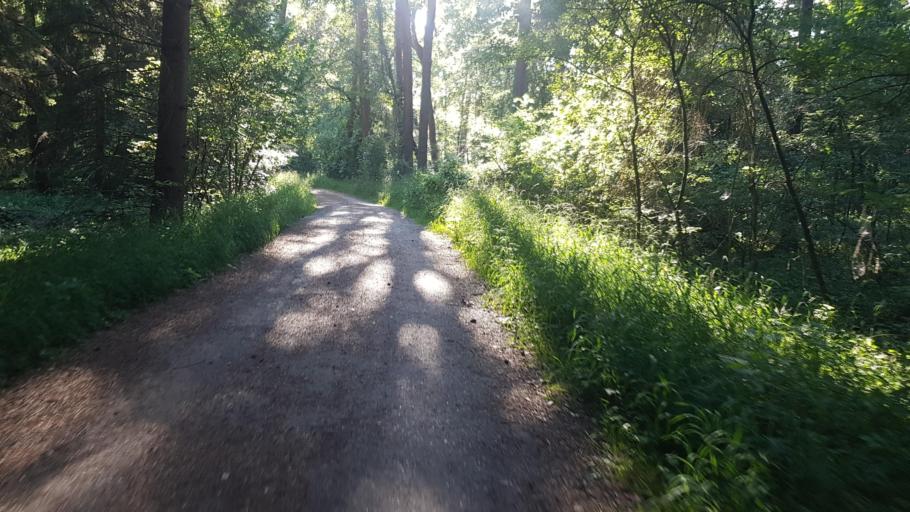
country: DE
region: Bavaria
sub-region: Upper Bavaria
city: Karlsfeld
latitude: 48.2439
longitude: 11.4956
